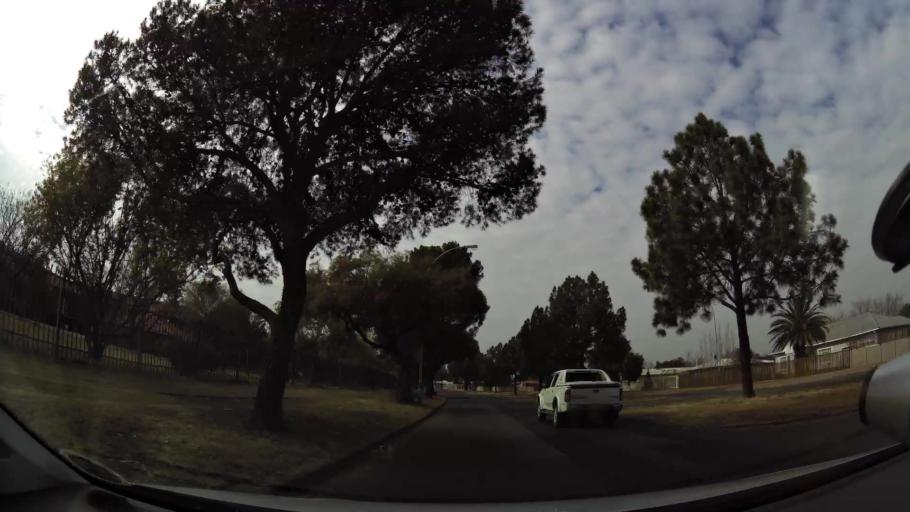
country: ZA
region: Orange Free State
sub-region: Mangaung Metropolitan Municipality
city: Bloemfontein
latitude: -29.1303
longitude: 26.1937
